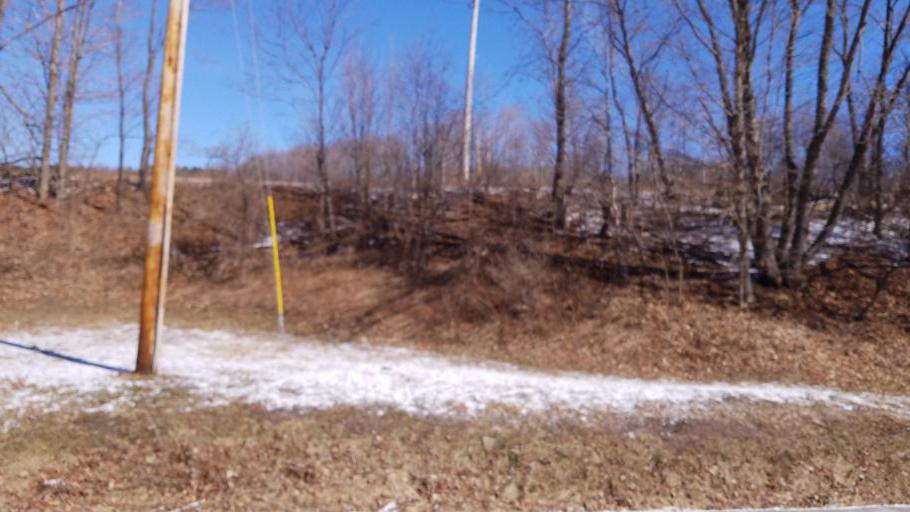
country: US
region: New York
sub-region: Allegany County
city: Andover
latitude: 42.0665
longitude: -77.8360
